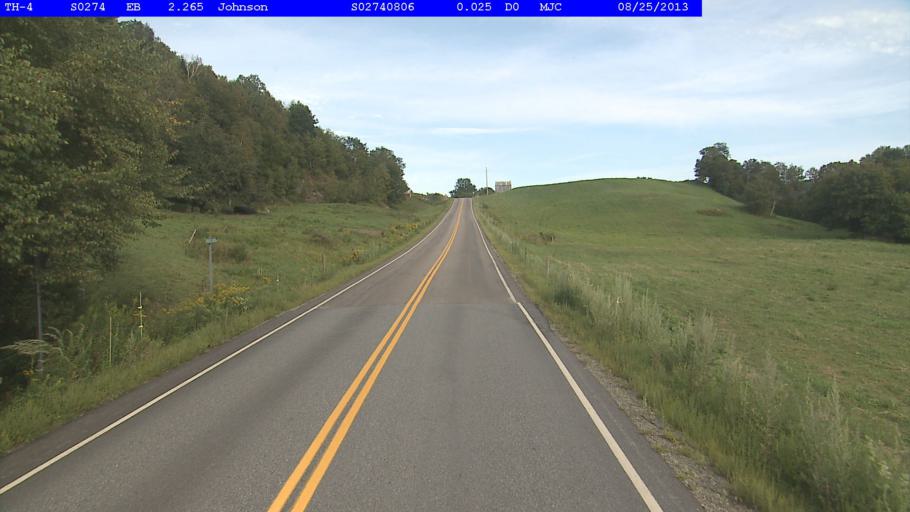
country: US
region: Vermont
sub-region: Lamoille County
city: Johnson
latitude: 44.6562
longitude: -72.7505
